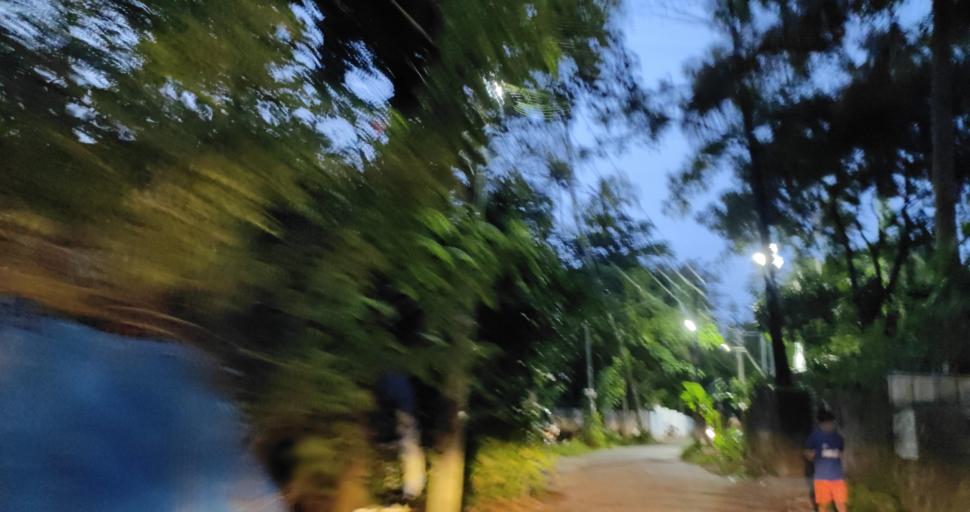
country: IN
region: Kerala
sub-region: Alappuzha
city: Vayalar
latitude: 9.7203
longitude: 76.2913
